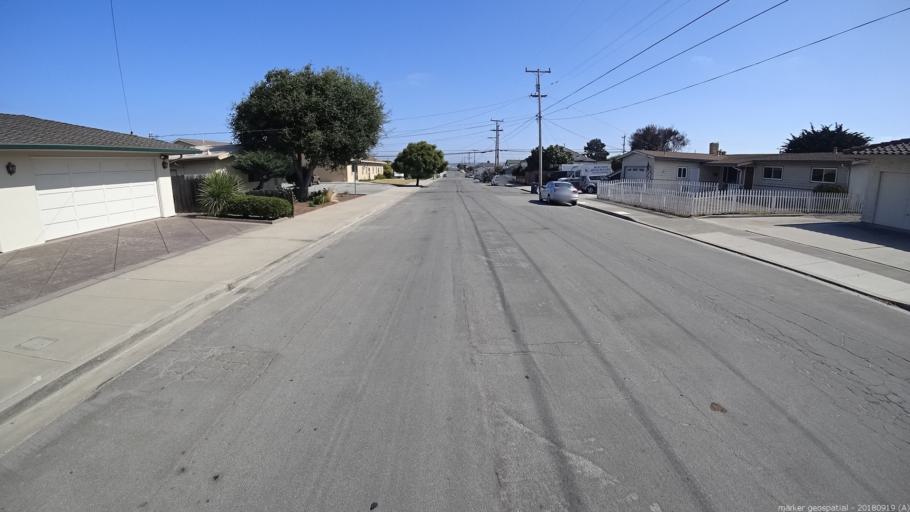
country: US
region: California
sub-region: Monterey County
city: Castroville
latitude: 36.7660
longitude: -121.7532
